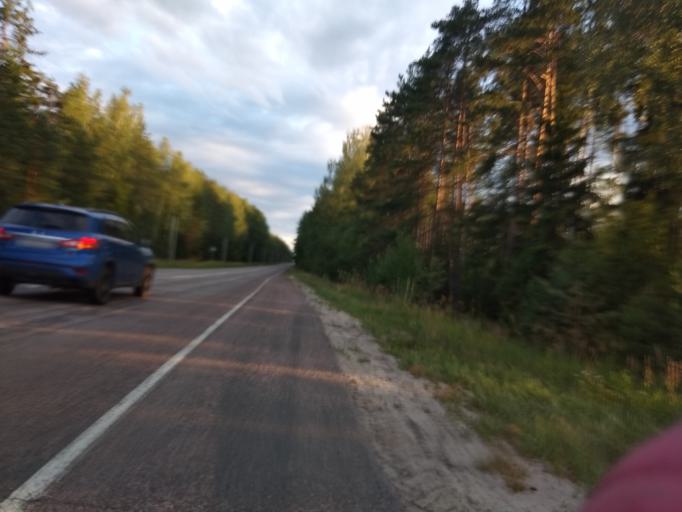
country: RU
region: Moskovskaya
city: Misheronskiy
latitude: 55.6174
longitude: 39.7249
